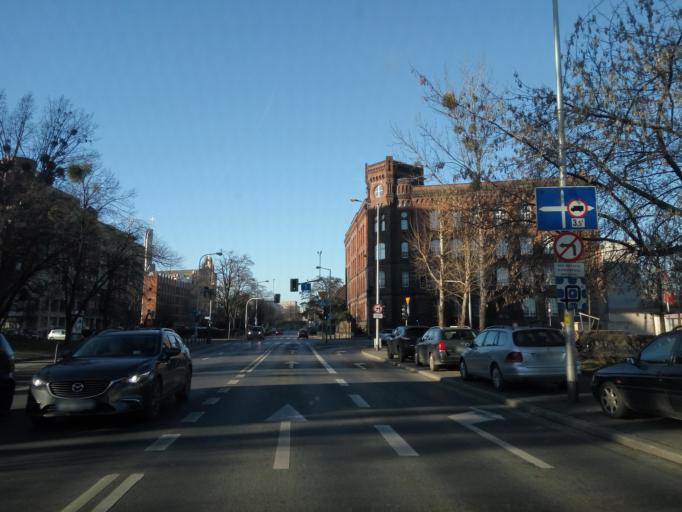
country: PL
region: Lower Silesian Voivodeship
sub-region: Powiat wroclawski
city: Wroclaw
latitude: 51.1001
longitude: 17.0240
